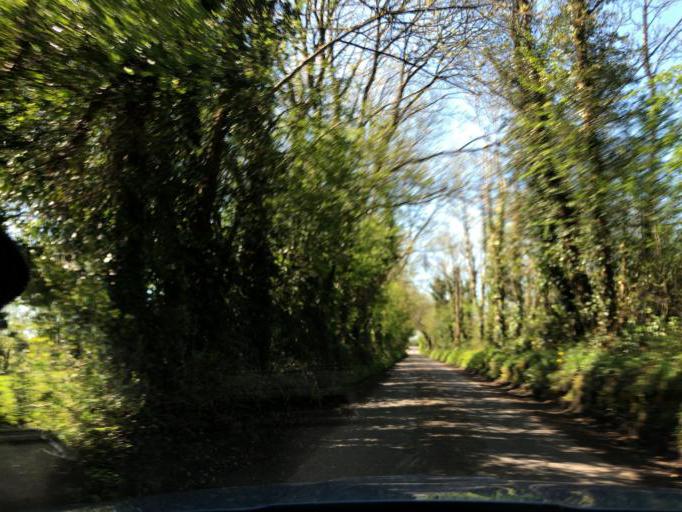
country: IE
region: Connaught
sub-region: County Galway
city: Portumna
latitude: 53.1528
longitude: -8.3359
